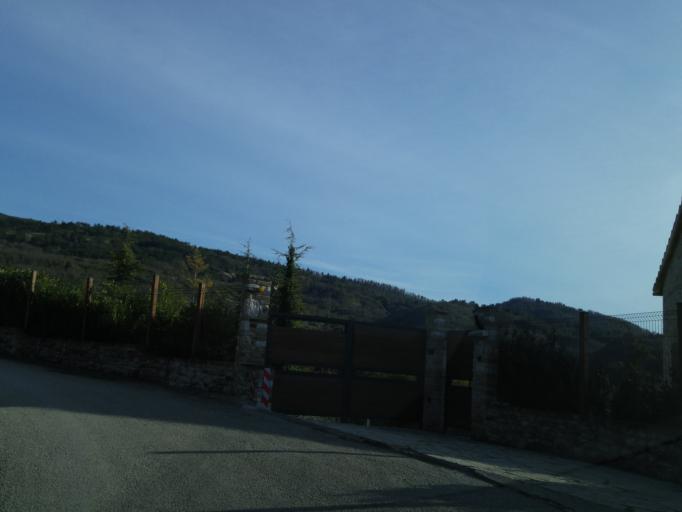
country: IT
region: The Marches
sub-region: Provincia di Pesaro e Urbino
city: Fermignano
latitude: 43.6771
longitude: 12.6764
